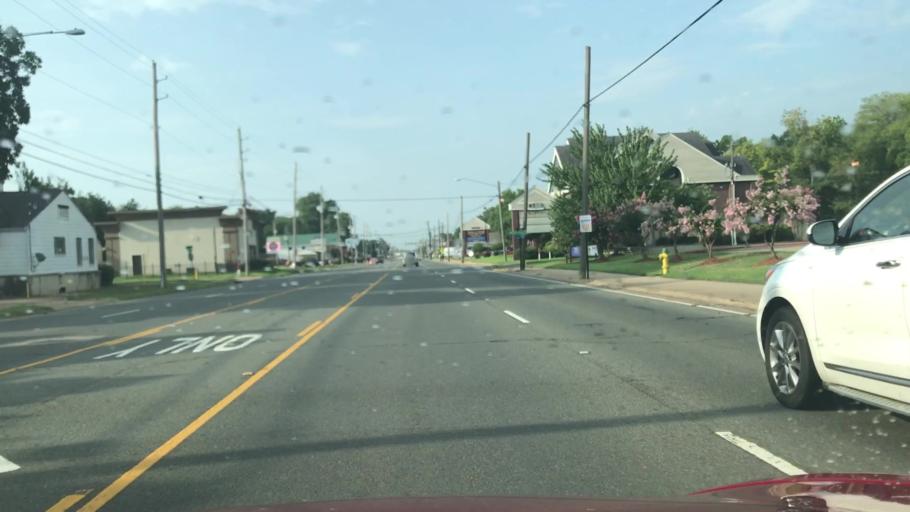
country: US
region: Louisiana
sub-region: Bossier Parish
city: Bossier City
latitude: 32.4630
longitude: -93.7222
